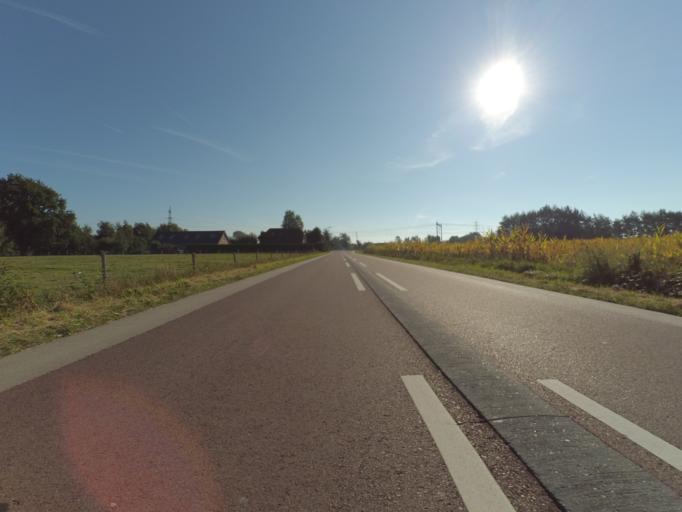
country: NL
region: Gelderland
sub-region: Gemeente Putten
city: Putten
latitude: 52.2611
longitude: 5.5674
